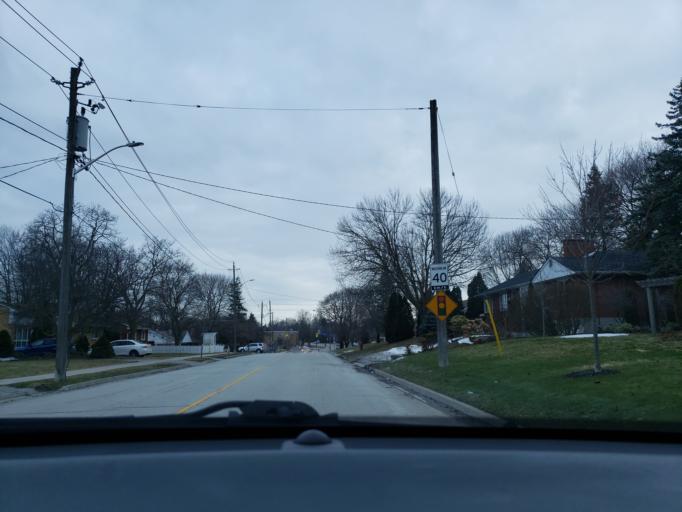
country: CA
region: Ontario
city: Newmarket
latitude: 44.0483
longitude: -79.4717
